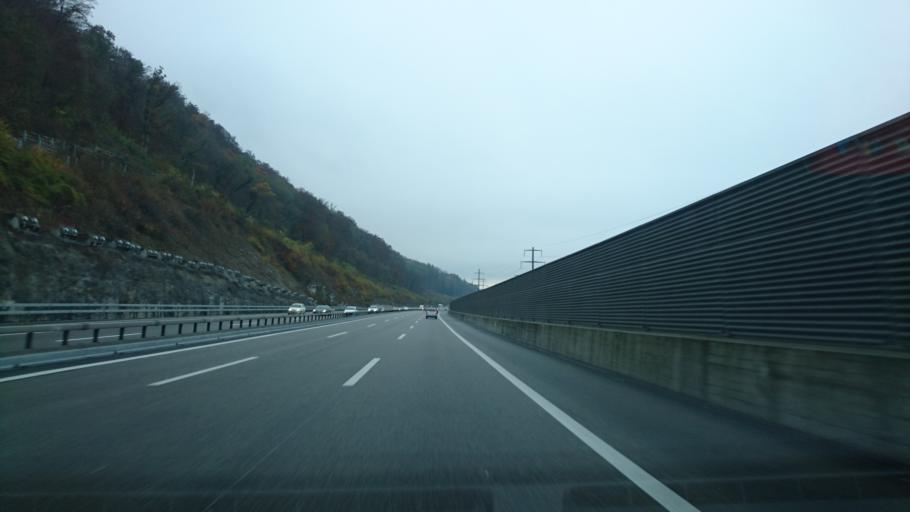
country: CH
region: Aargau
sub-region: Bezirk Zofingen
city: Rothrist
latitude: 47.3120
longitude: 7.8694
